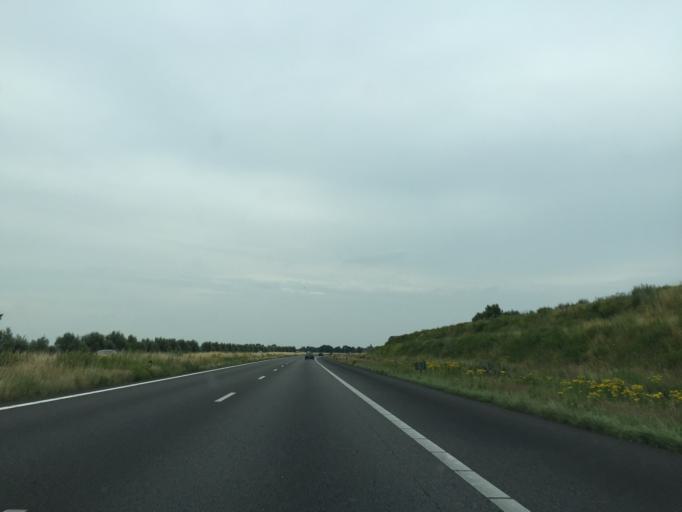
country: NL
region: North Brabant
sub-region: Gemeente Landerd
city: Schaijk
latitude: 51.7724
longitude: 5.6321
